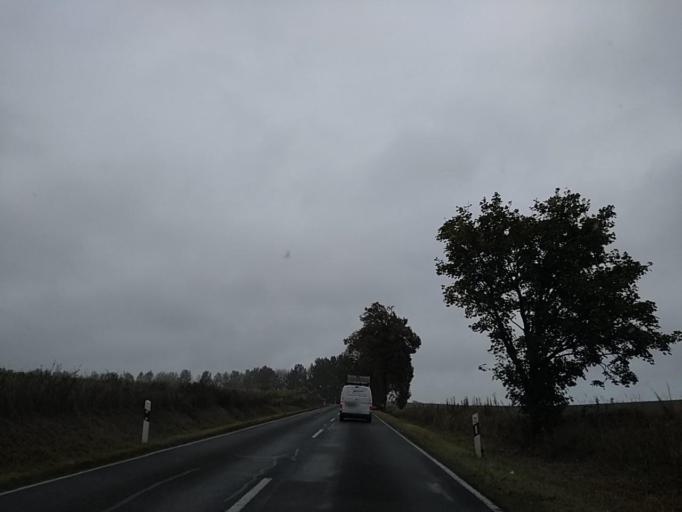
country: DE
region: Mecklenburg-Vorpommern
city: Kropelin
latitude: 54.0848
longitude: 11.7845
